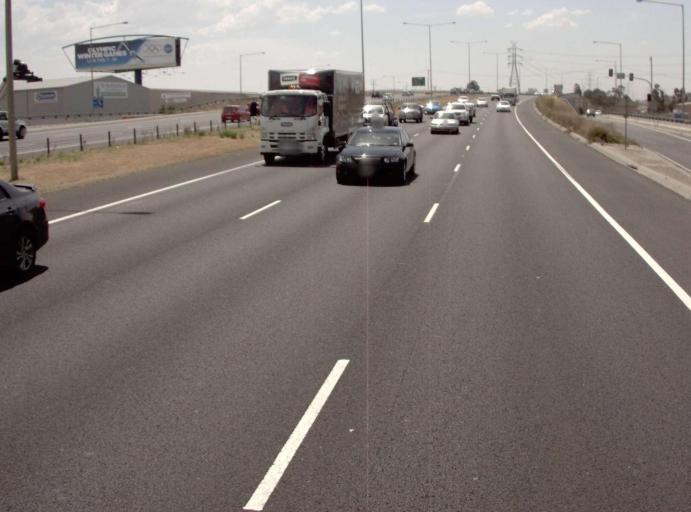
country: AU
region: Victoria
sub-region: Brimbank
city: Sunshine West
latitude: -37.8192
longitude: 144.8095
